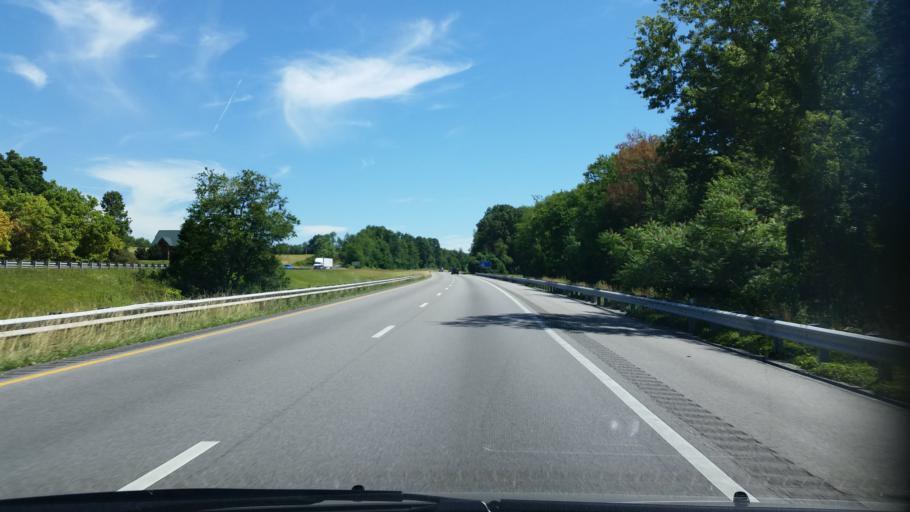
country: US
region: Virginia
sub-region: Washington County
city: Abingdon
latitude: 36.7298
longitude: -81.9074
